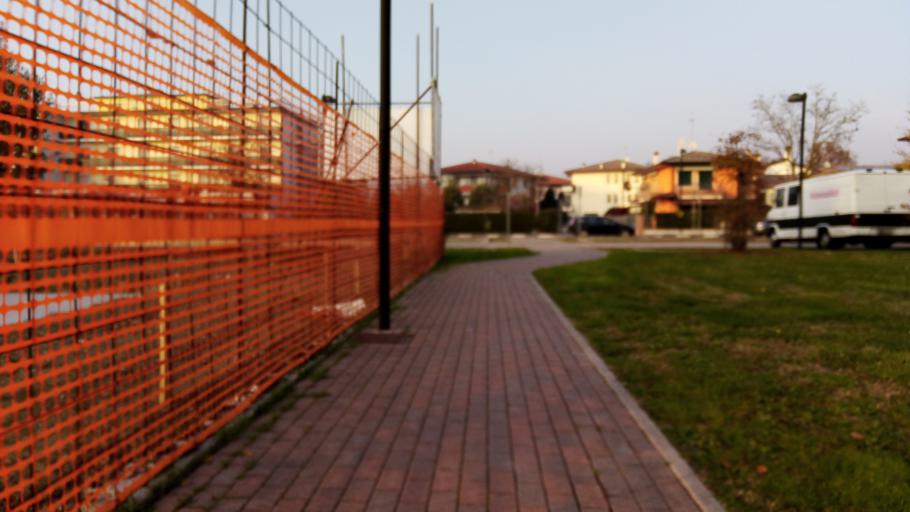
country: IT
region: Veneto
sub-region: Provincia di Padova
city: Abano Terme
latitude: 45.3544
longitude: 11.7691
